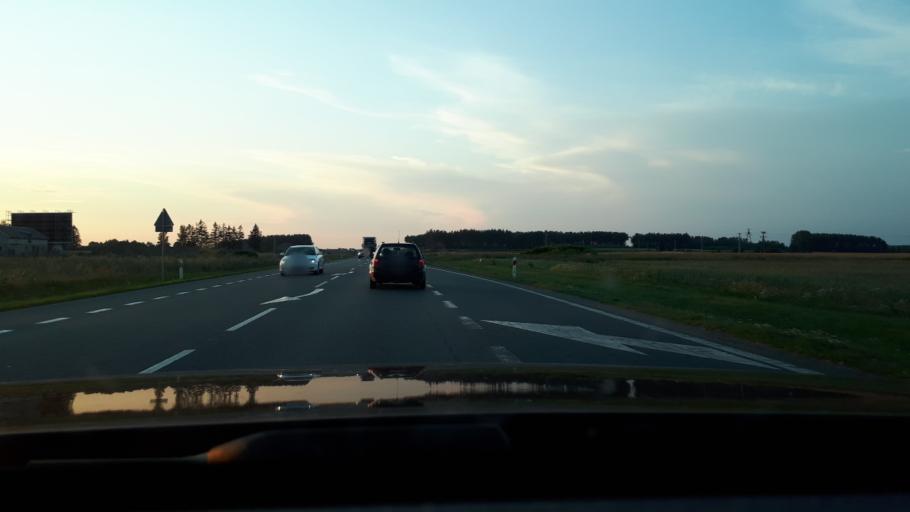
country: PL
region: Masovian Voivodeship
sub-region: Powiat mlawski
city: Wieczfnia Koscielna
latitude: 53.2017
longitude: 20.4352
